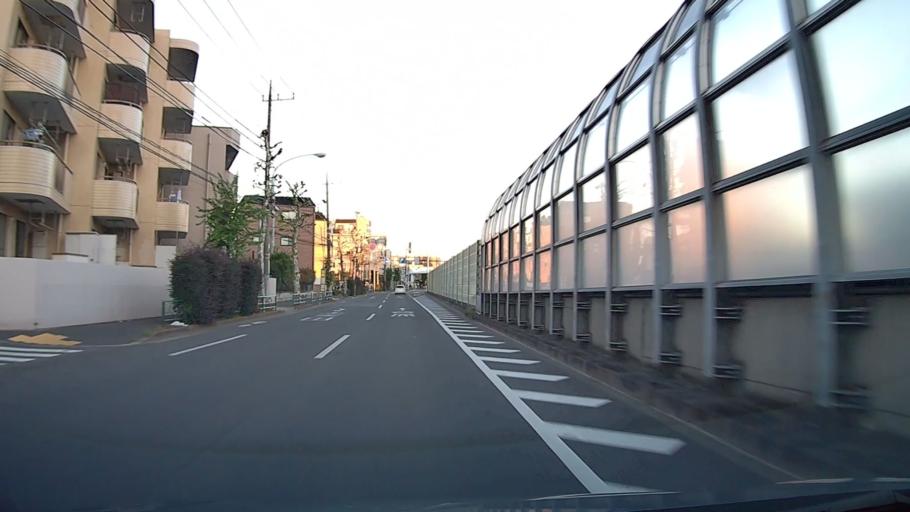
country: JP
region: Saitama
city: Wako
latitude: 35.7552
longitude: 139.6056
